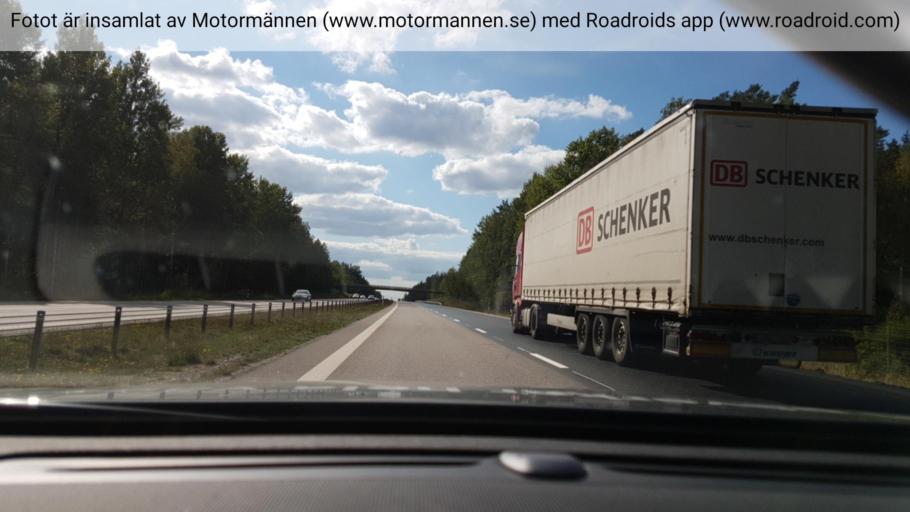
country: SE
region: OEstergoetland
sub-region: Linkopings Kommun
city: Vikingstad
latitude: 58.3831
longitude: 15.3605
